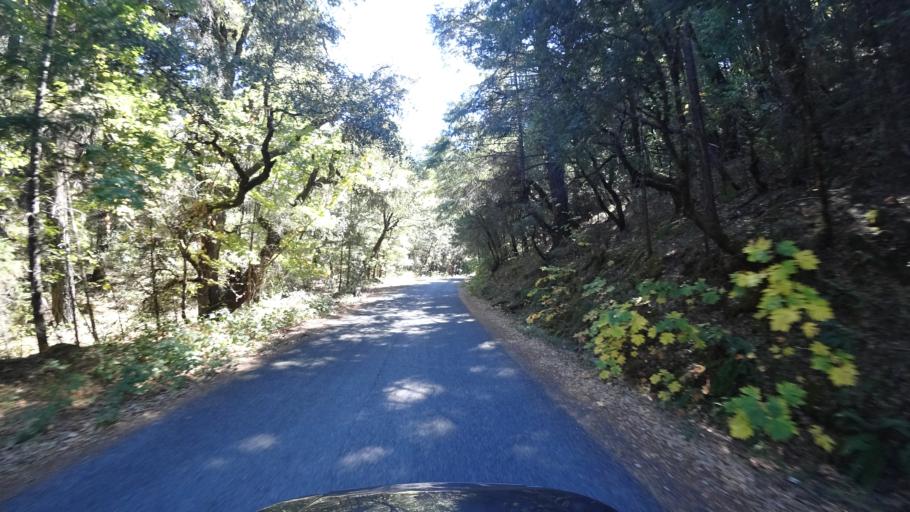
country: US
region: California
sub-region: Siskiyou County
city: Happy Camp
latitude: 41.3816
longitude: -123.4931
